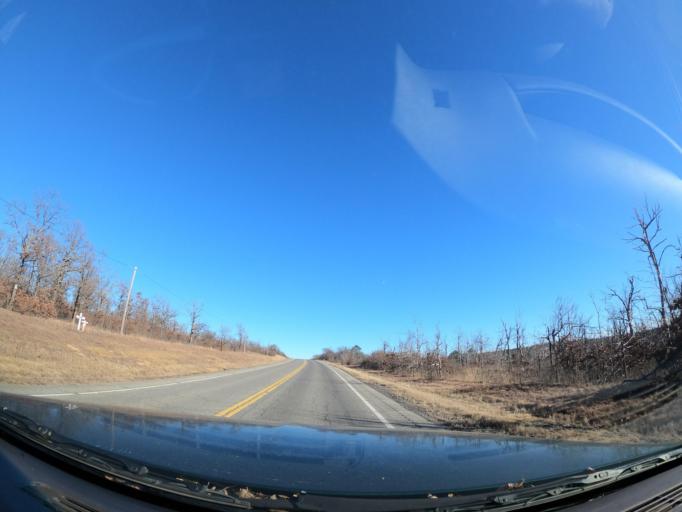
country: US
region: Oklahoma
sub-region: Pittsburg County
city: Longtown
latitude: 35.2254
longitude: -95.4436
